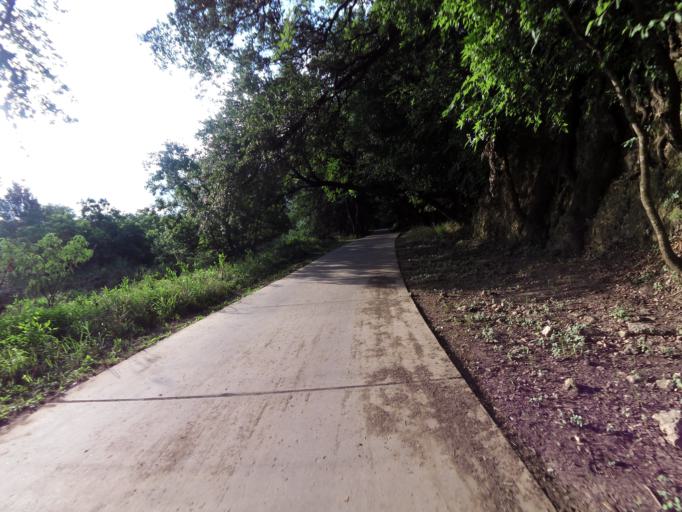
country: US
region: Texas
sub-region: Bexar County
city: Leon Valley
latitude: 29.5265
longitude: -98.6306
